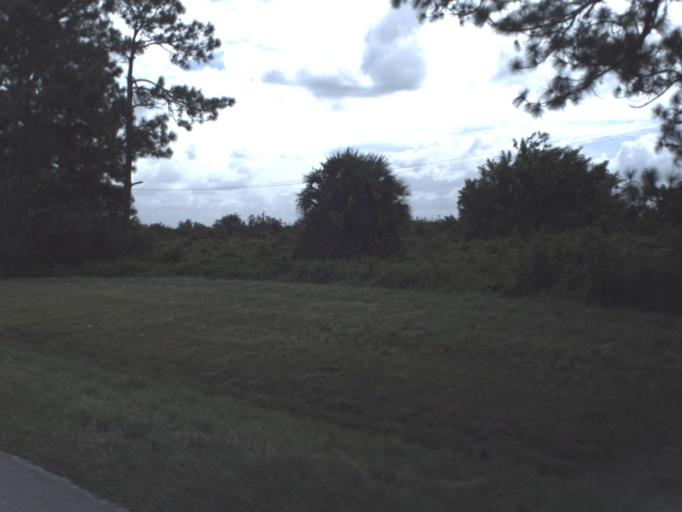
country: US
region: Florida
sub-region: Collier County
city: Immokalee
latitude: 26.4992
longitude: -81.4883
